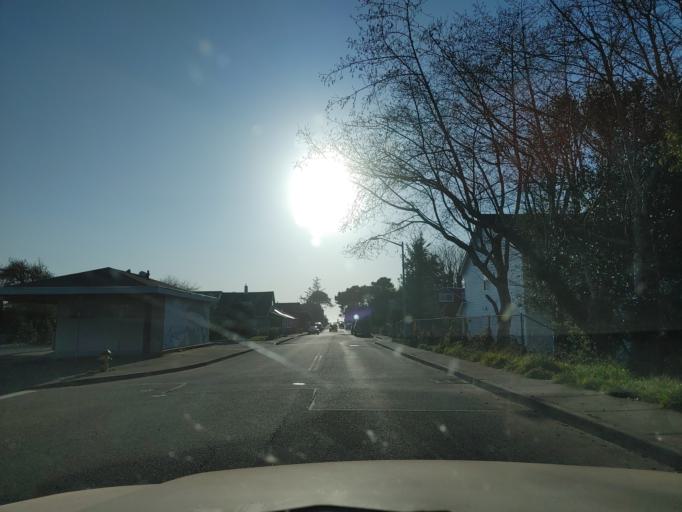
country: US
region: Oregon
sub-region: Clatsop County
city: Seaside
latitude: 46.0015
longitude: -123.9228
